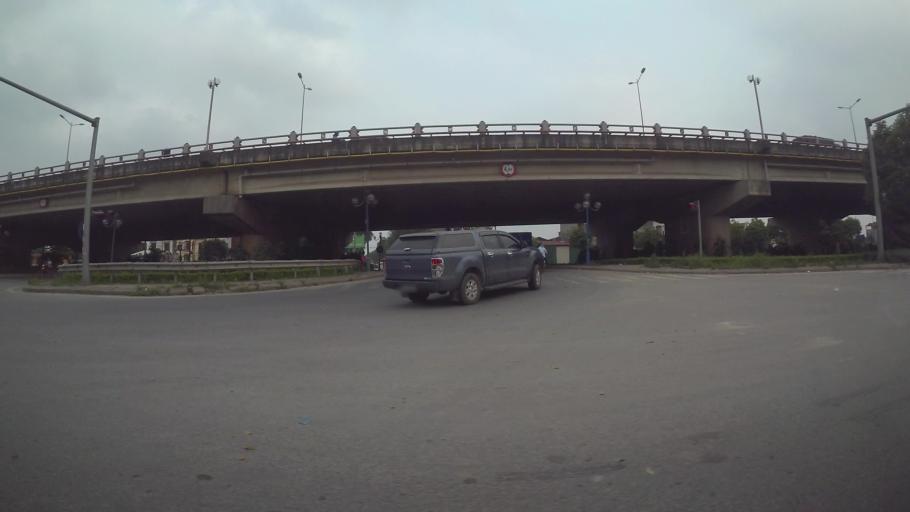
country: VN
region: Ha Noi
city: Trau Quy
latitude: 21.0042
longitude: 105.9107
